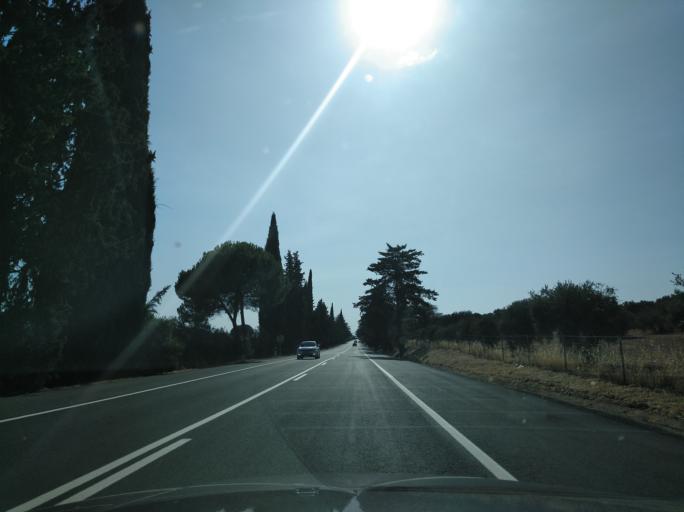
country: ES
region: Andalusia
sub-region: Provincia de Huelva
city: Rosal de la Frontera
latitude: 37.9516
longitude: -7.2925
